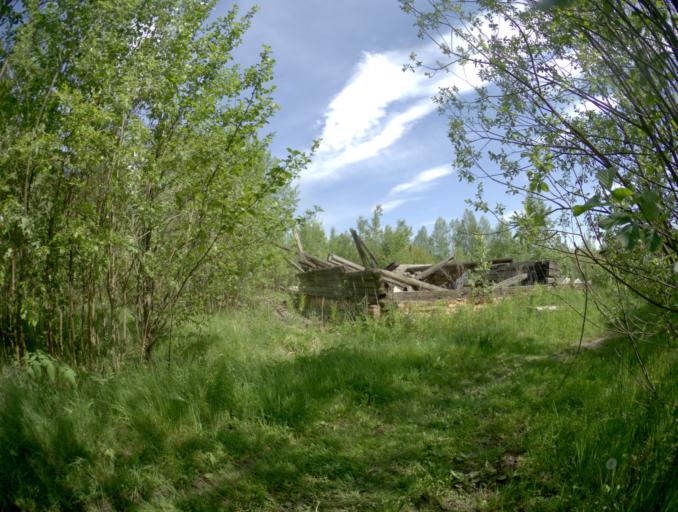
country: RU
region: Vladimir
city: Ivanishchi
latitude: 55.6670
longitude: 40.3881
